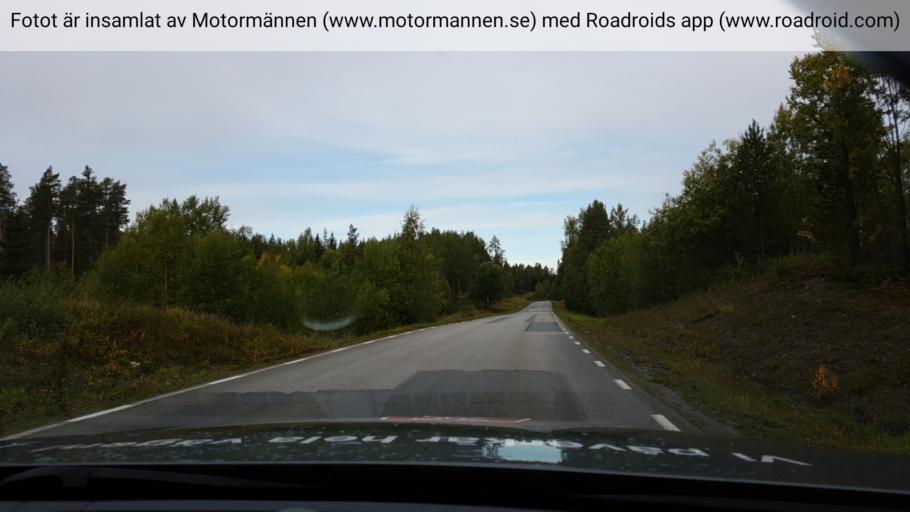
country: SE
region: Jaemtland
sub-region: Krokoms Kommun
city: Krokom
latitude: 63.2844
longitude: 14.2674
